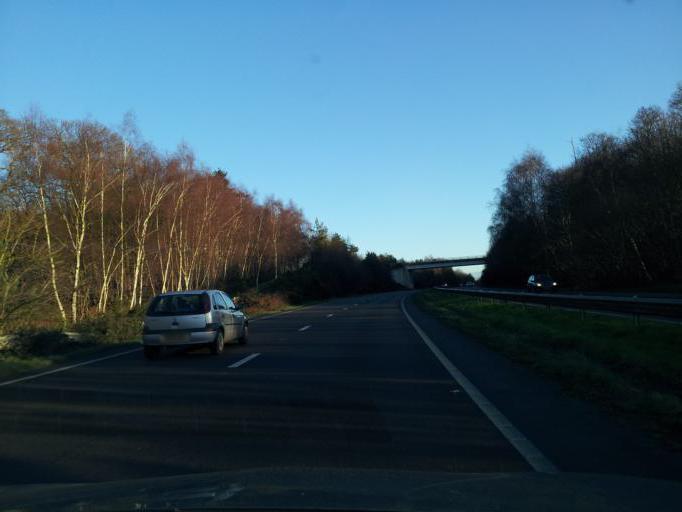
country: GB
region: England
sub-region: Suffolk
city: Kesgrave
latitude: 52.0776
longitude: 1.2690
